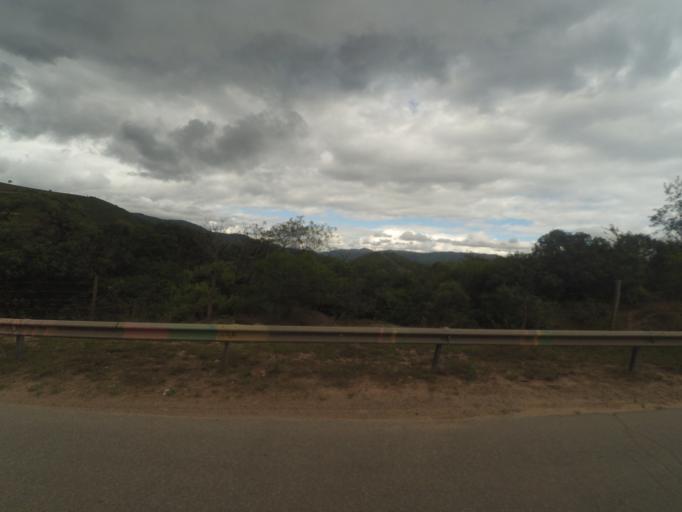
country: BO
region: Santa Cruz
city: Samaipata
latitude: -18.1757
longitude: -63.8581
